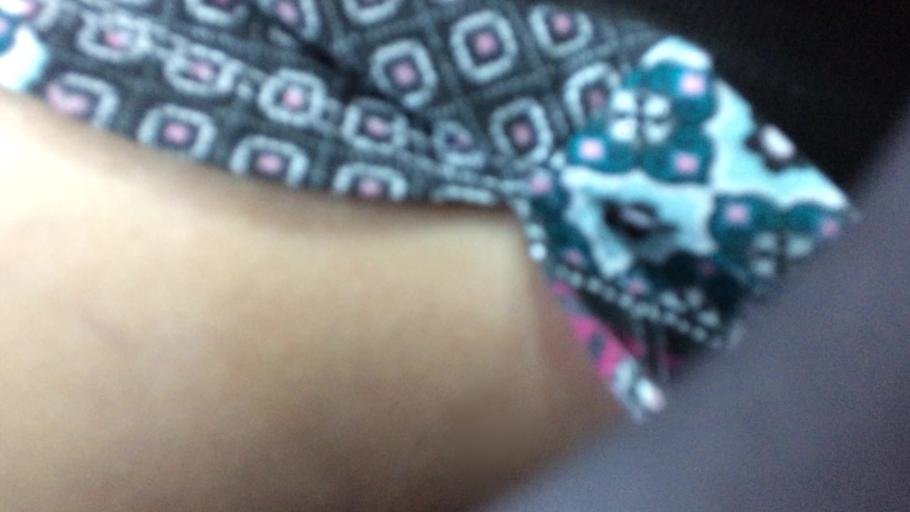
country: US
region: New Mexico
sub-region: San Miguel County
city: Las Vegas
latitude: 35.8297
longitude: -104.9651
